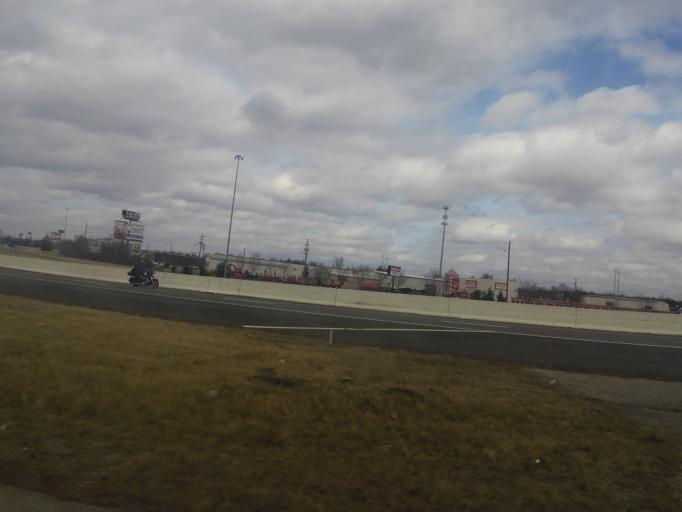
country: US
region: Tennessee
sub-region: Rutherford County
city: Murfreesboro
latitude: 35.8093
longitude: -86.3940
